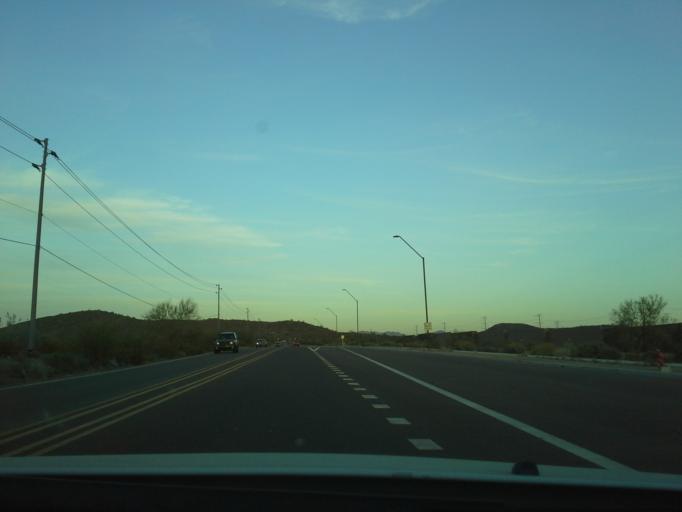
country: US
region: Arizona
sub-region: Maricopa County
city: Anthem
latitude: 33.7129
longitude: -112.0783
